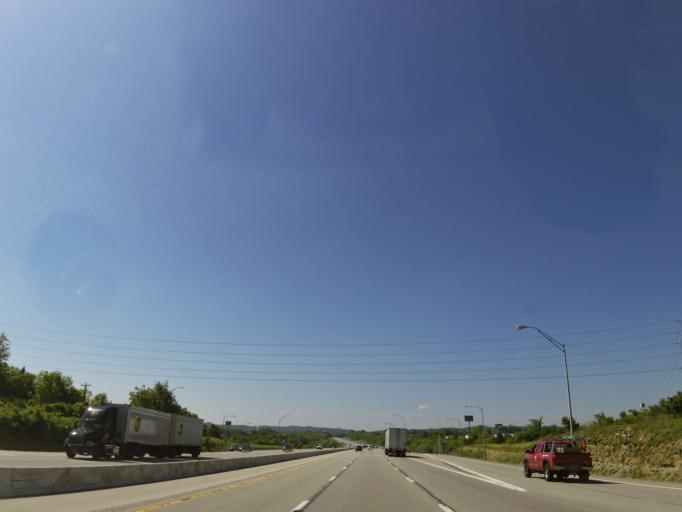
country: US
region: Kentucky
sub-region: Madison County
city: Berea
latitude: 37.6014
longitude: -84.3145
